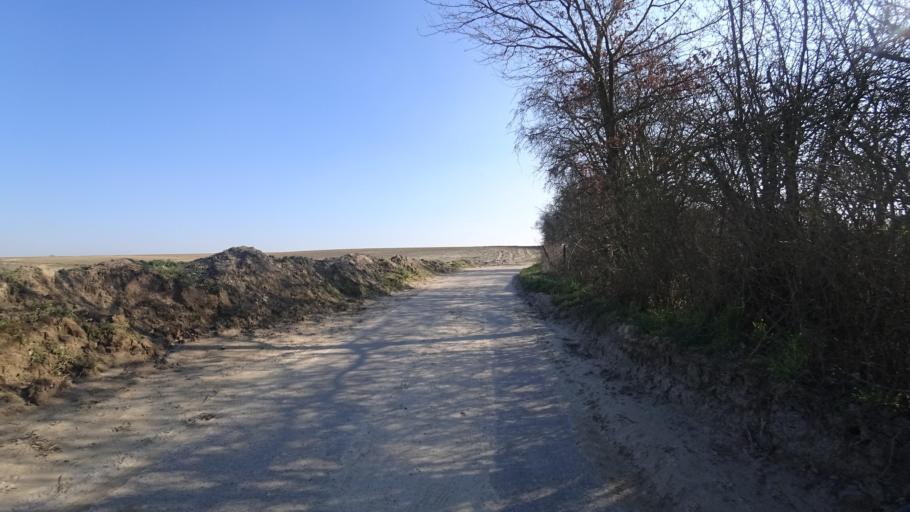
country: BE
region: Wallonia
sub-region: Province du Brabant Wallon
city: Chastre
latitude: 50.5962
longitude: 4.6117
